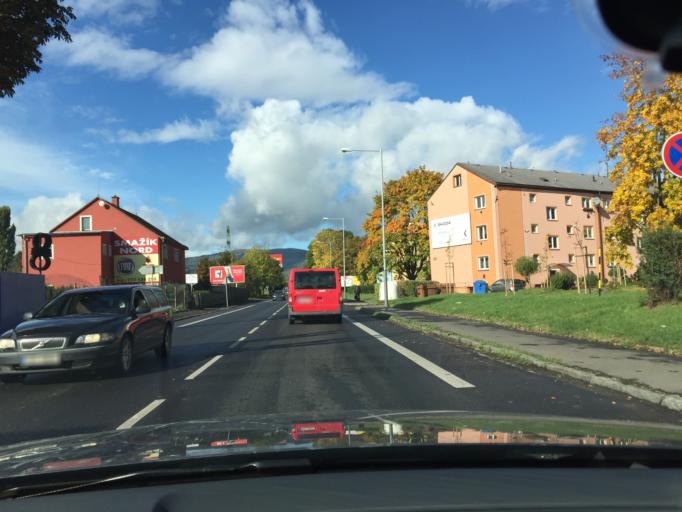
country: CZ
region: Ustecky
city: Trmice
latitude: 50.6863
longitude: 13.9920
